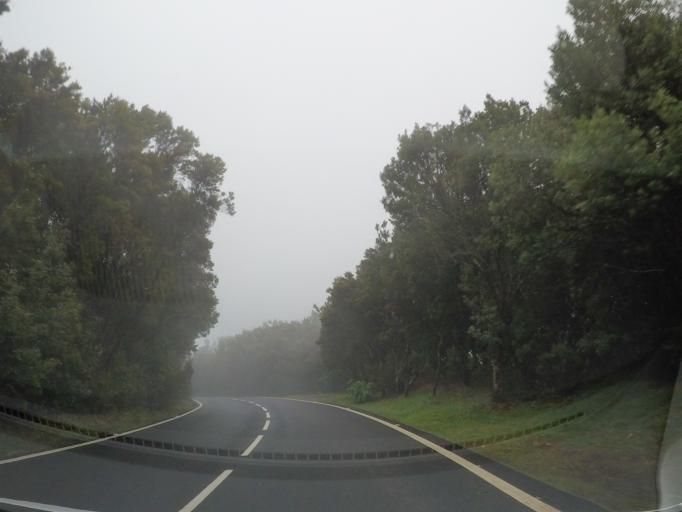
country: ES
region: Canary Islands
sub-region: Provincia de Santa Cruz de Tenerife
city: Vallehermosa
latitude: 28.1253
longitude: -17.2555
